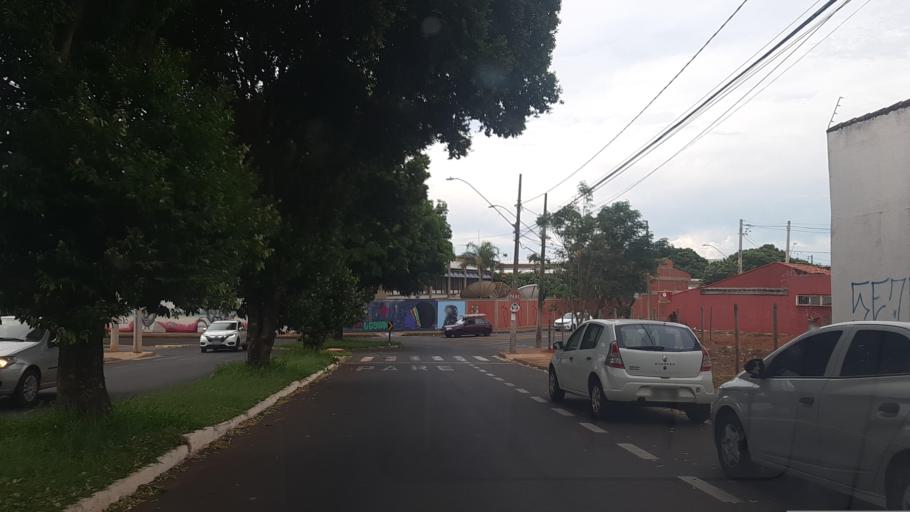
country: BR
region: Minas Gerais
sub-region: Uberlandia
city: Uberlandia
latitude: -18.9198
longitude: -48.2543
